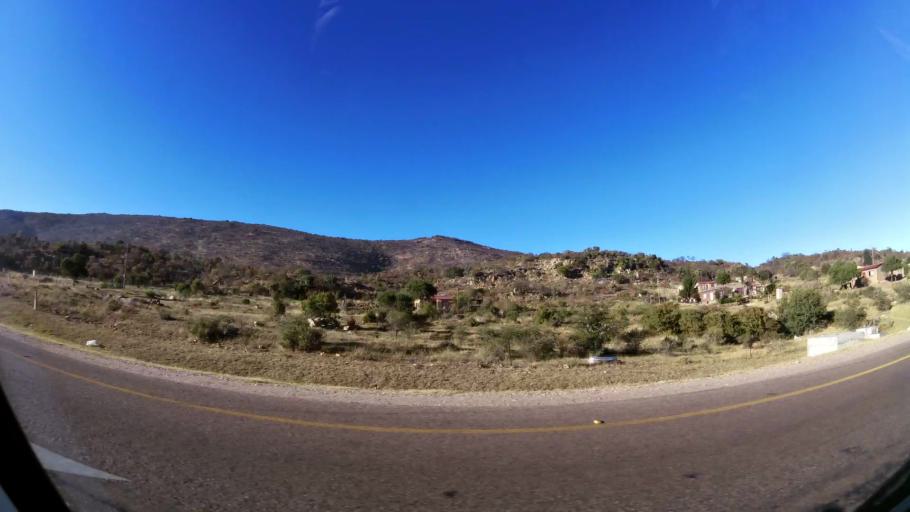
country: ZA
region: Limpopo
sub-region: Capricorn District Municipality
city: Mankoeng
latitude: -23.9430
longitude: 29.8200
